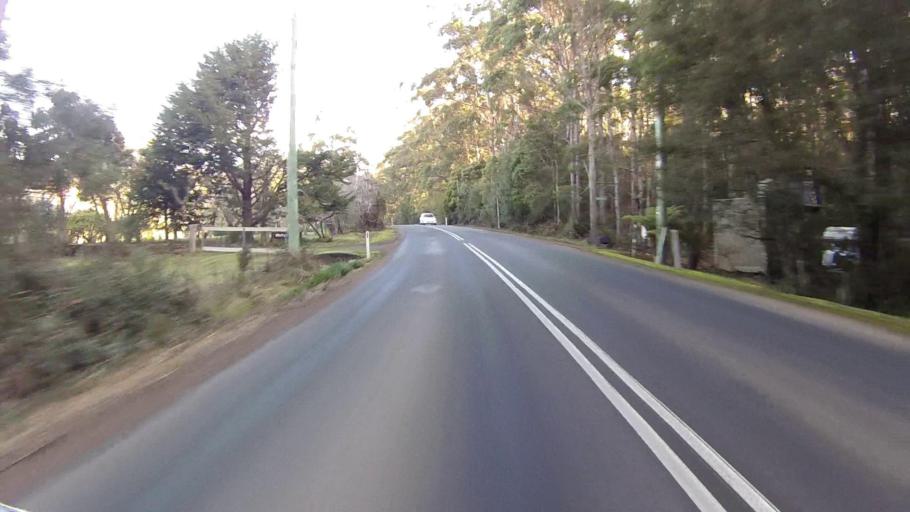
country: AU
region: Tasmania
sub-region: Clarence
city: Sandford
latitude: -43.1193
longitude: 147.8509
